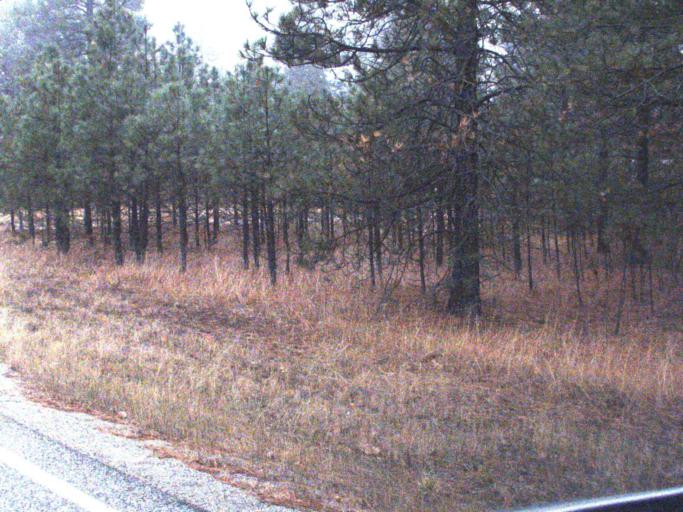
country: CA
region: British Columbia
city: Grand Forks
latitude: 48.9889
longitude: -118.2251
